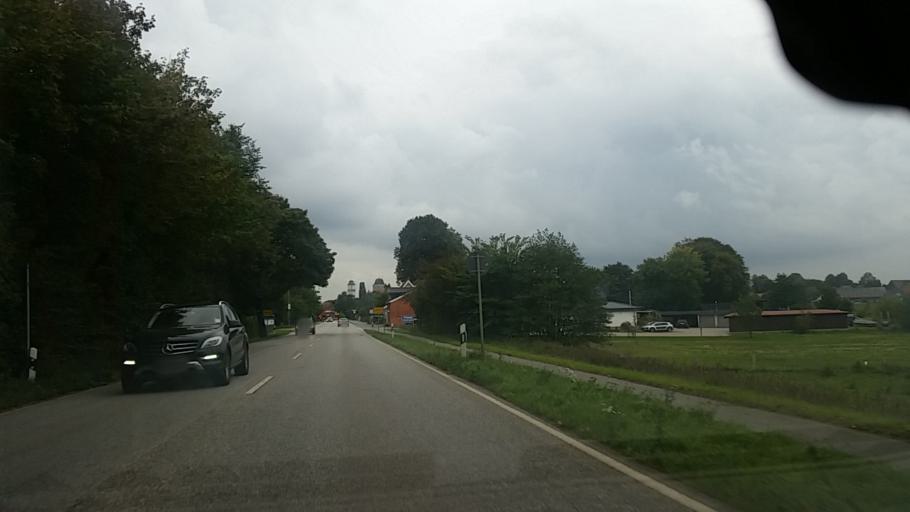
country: DE
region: Schleswig-Holstein
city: Leezen
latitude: 53.8718
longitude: 10.2581
